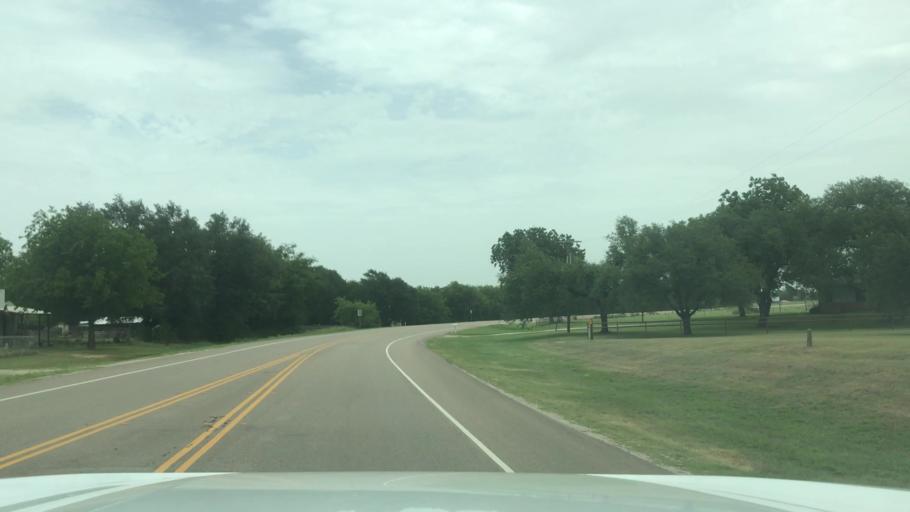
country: US
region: Texas
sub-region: Hamilton County
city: Hico
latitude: 31.9823
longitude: -97.8689
